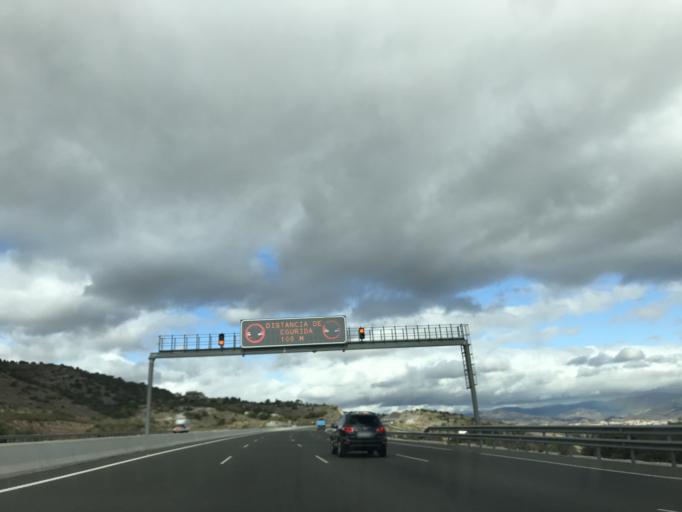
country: ES
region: Andalusia
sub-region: Provincia de Malaga
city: Torremolinos
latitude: 36.6387
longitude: -4.5143
